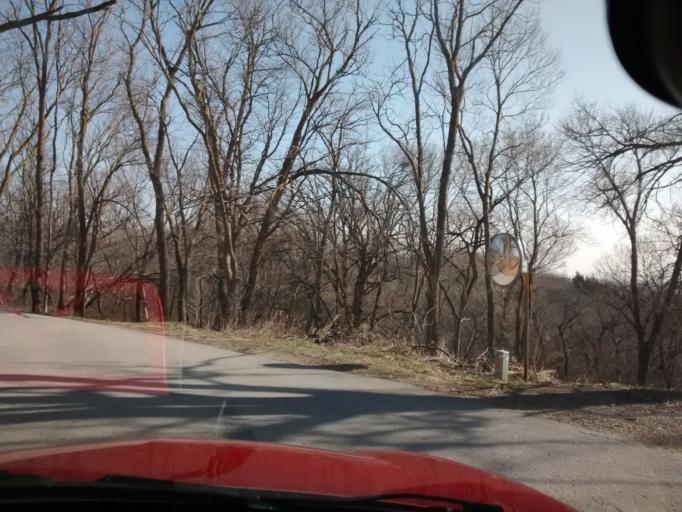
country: US
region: Iowa
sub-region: Pottawattamie County
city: Carter Lake
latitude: 41.4146
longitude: -95.8556
